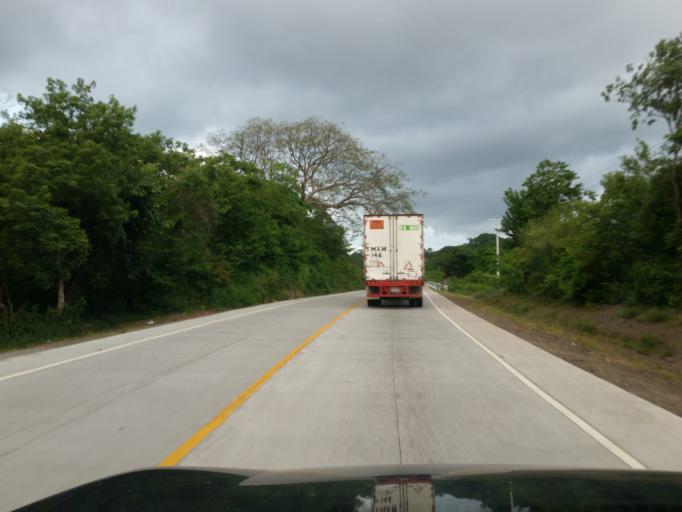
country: NI
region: Managua
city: Ciudad Sandino
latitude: 12.0831
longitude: -86.3944
